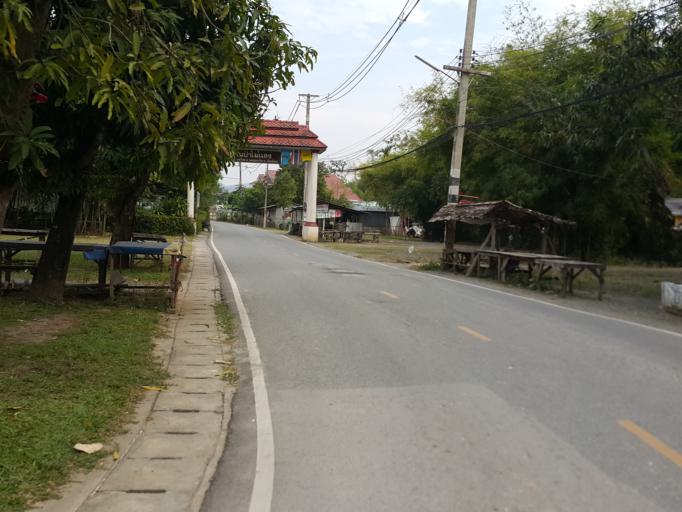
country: TH
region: Chiang Mai
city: San Kamphaeng
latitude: 18.8347
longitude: 99.1567
